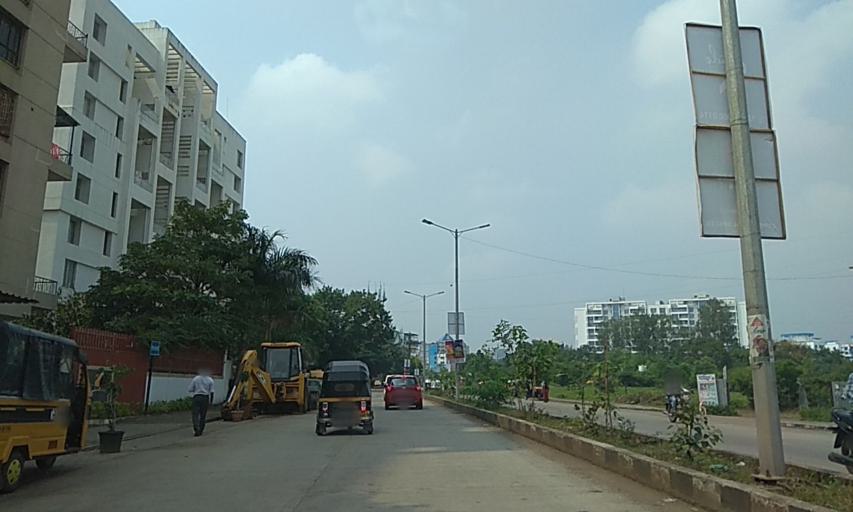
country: IN
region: Maharashtra
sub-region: Pune Division
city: Pimpri
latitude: 18.5597
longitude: 73.7805
